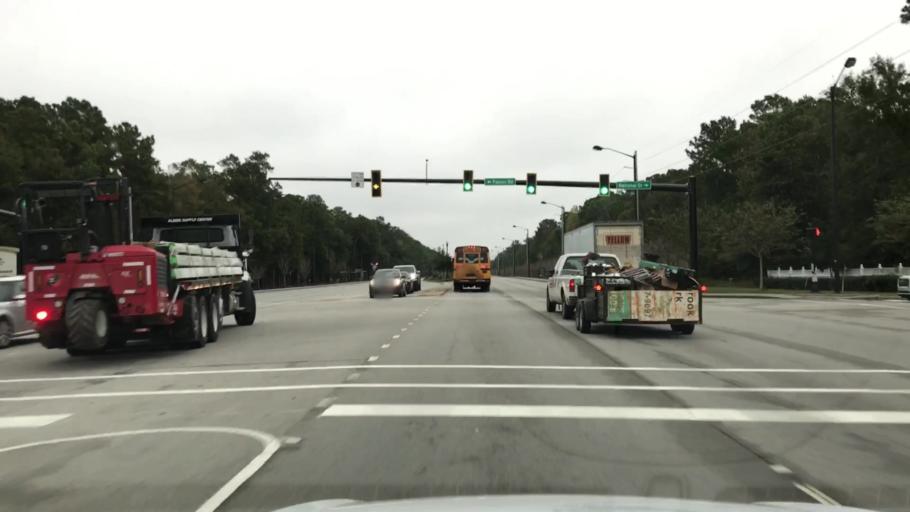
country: US
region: South Carolina
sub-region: Charleston County
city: Isle of Palms
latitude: 32.8752
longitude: -79.7710
